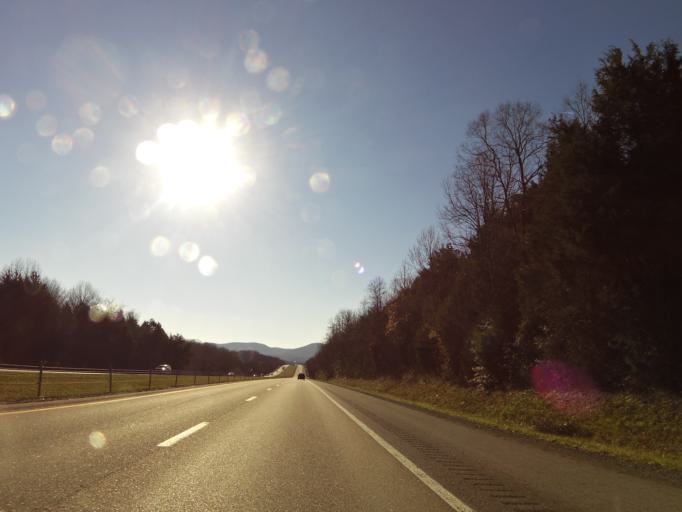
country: US
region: Tennessee
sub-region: Jefferson County
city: White Pine
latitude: 36.0165
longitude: -83.2961
